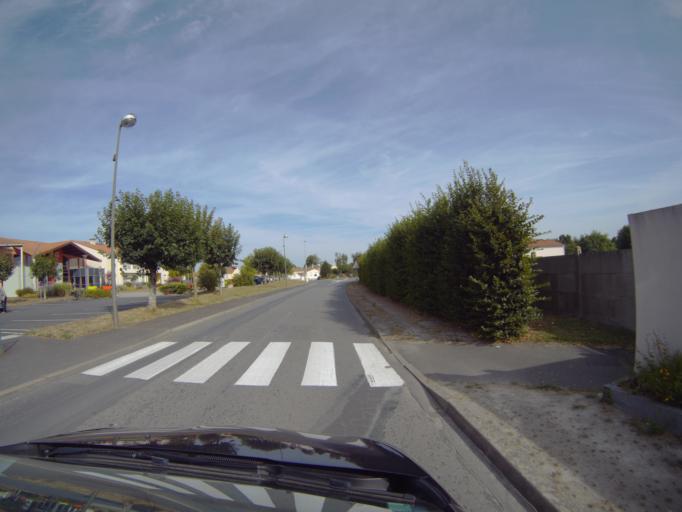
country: FR
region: Pays de la Loire
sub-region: Departement de la Vendee
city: Saint-Andre-Treize-Voies
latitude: 46.9112
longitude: -1.3802
